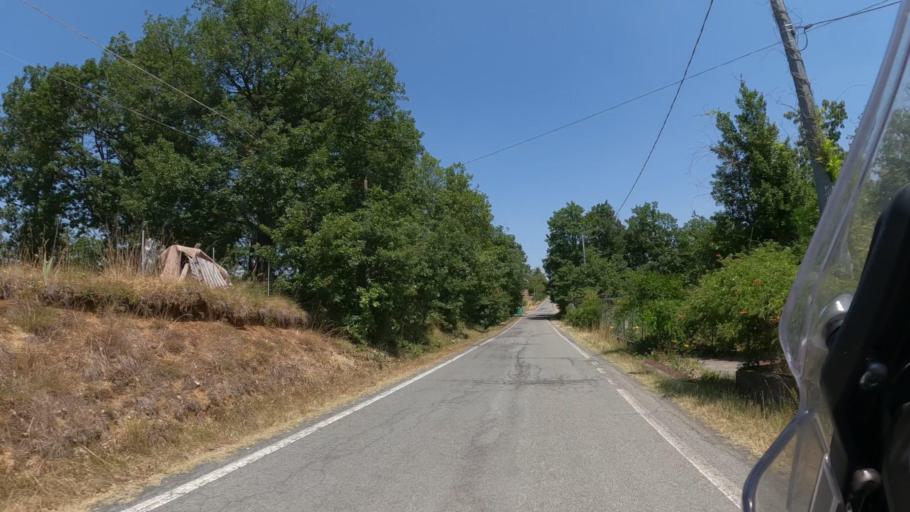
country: IT
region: Piedmont
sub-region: Provincia di Alessandria
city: Morbello
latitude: 44.5712
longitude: 8.5186
